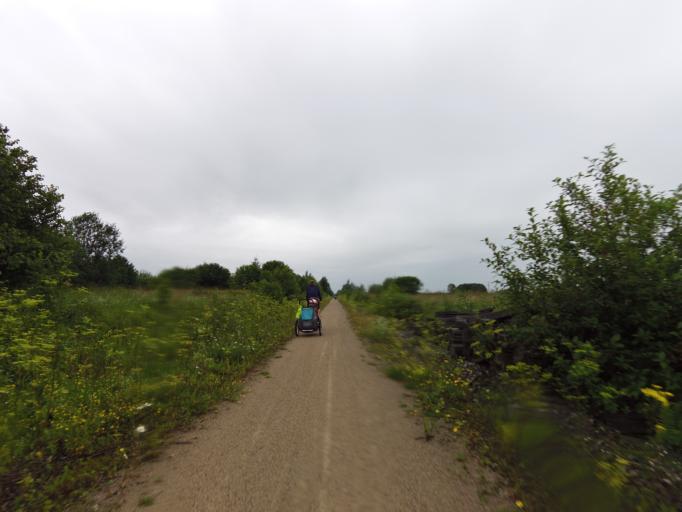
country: EE
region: Laeaene
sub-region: Ridala Parish
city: Uuemoisa
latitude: 58.9538
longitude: 23.8148
